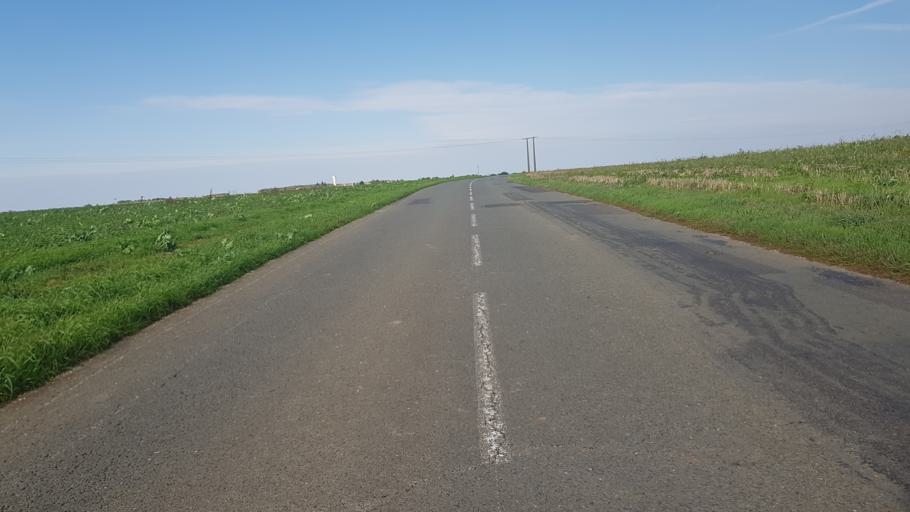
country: FR
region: Poitou-Charentes
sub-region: Departement de la Vienne
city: Chasseneuil-du-Poitou
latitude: 46.6488
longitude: 0.3488
